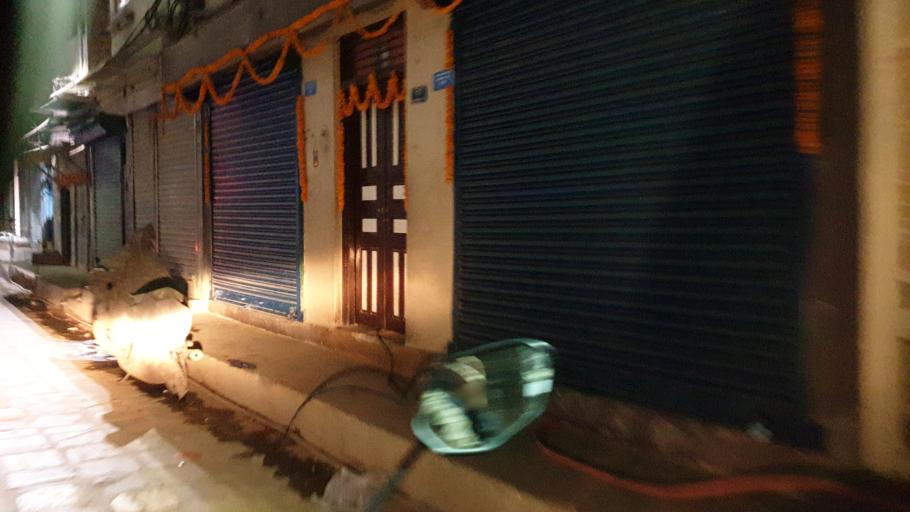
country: NP
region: Central Region
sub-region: Bagmati Zone
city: Kathmandu
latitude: 27.6985
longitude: 85.3078
